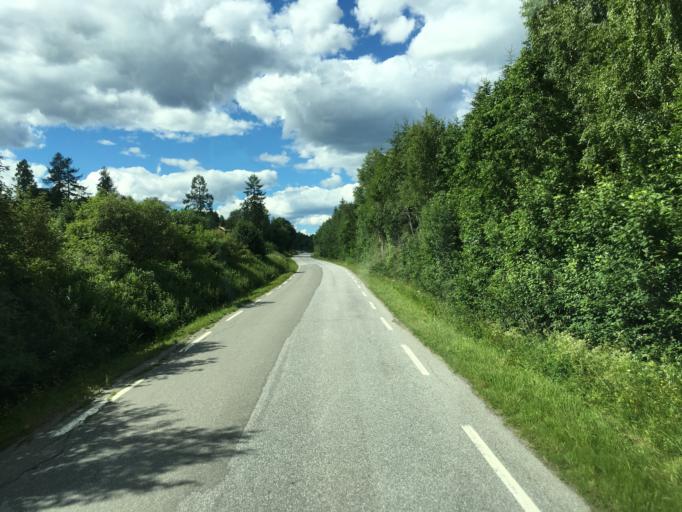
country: NO
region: Oppland
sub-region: Sondre Land
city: Hov
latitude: 60.6911
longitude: 10.2985
